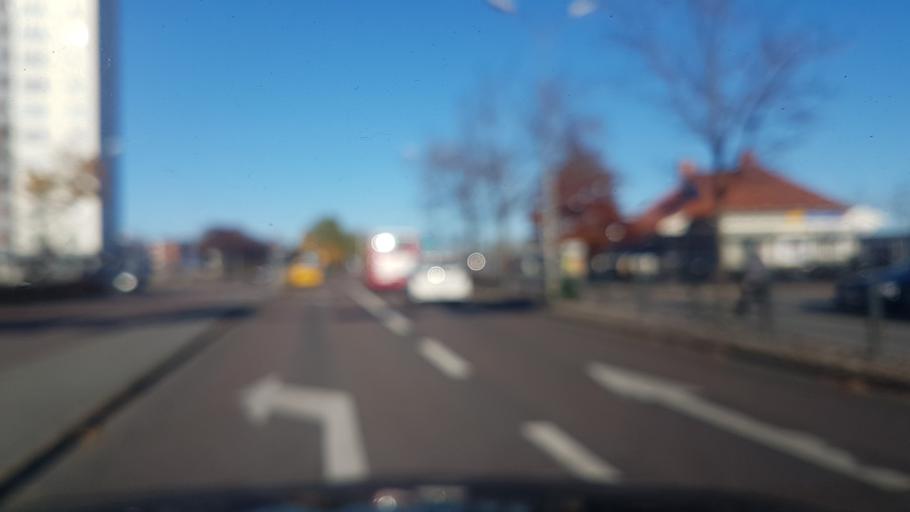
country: SE
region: Stockholm
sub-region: Sigtuna Kommun
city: Marsta
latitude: 59.6275
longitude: 17.8605
